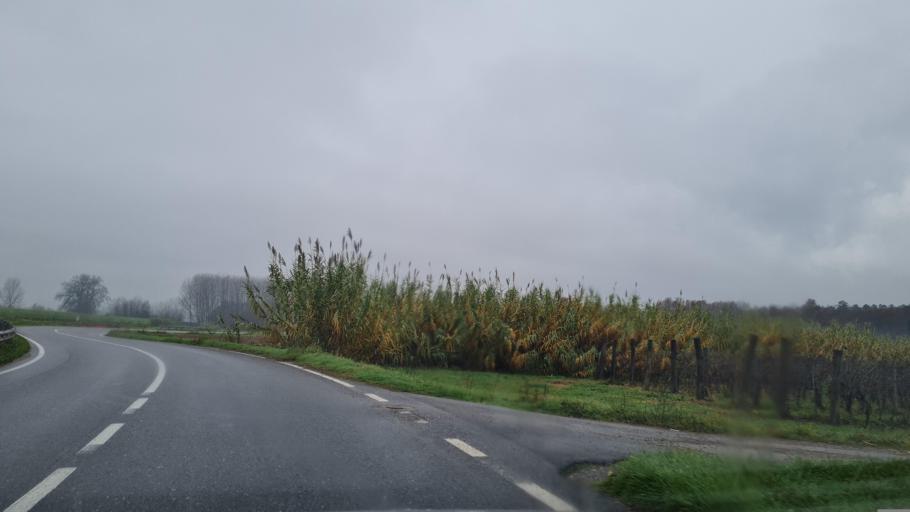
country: IT
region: Tuscany
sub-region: Provincia di Lucca
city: Lucca
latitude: 43.8599
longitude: 10.4609
